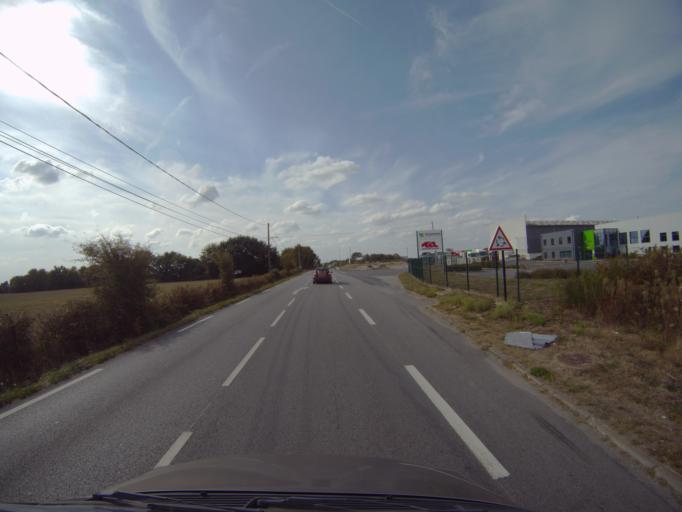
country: FR
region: Pays de la Loire
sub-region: Departement de la Loire-Atlantique
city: Sautron
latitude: 47.2443
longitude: -1.6827
